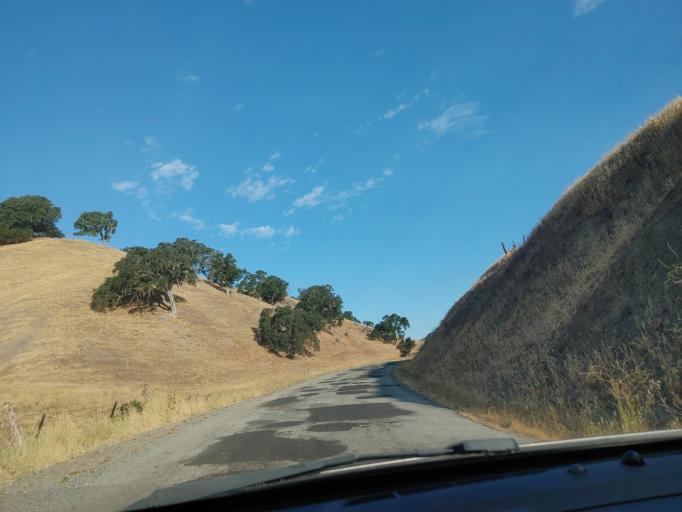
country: US
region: California
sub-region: San Benito County
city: Ridgemark
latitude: 36.7547
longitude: -121.1652
